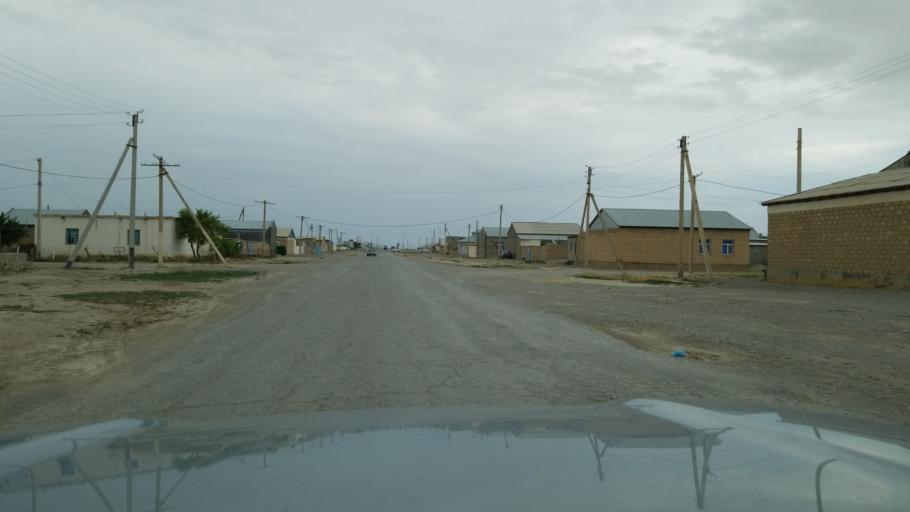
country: TM
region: Balkan
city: Serdar
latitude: 38.9924
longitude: 56.2781
